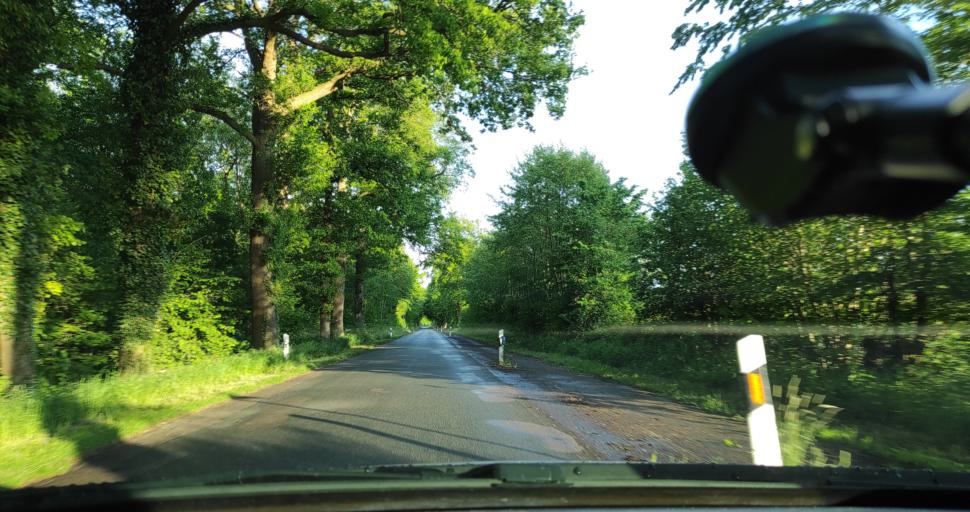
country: DE
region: North Rhine-Westphalia
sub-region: Regierungsbezirk Munster
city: Greven
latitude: 52.0852
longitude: 7.5691
